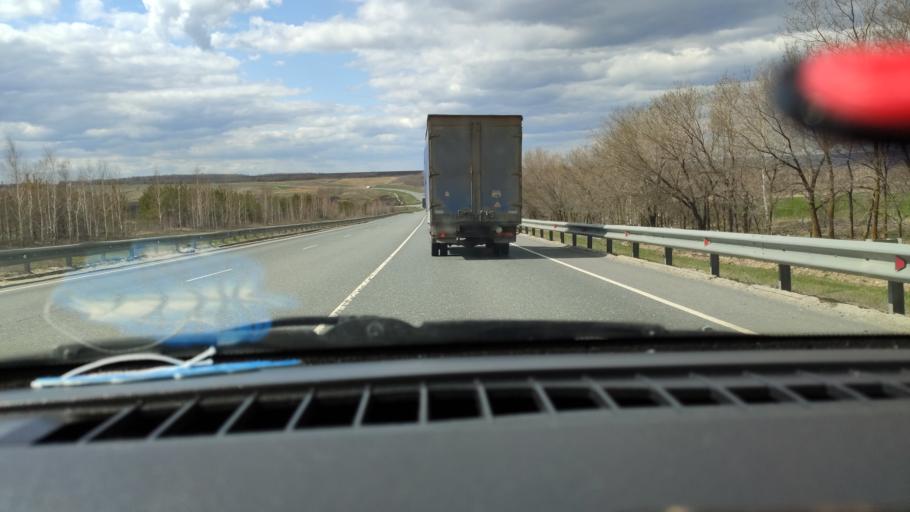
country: RU
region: Saratov
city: Balakovo
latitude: 52.1308
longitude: 47.7646
